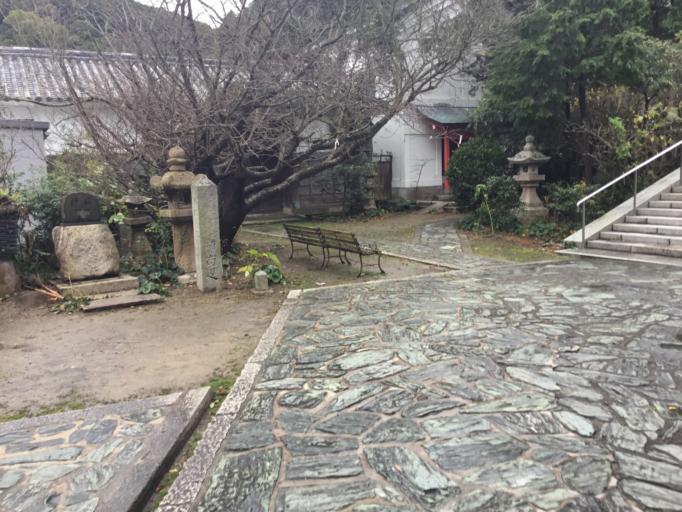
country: JP
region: Wakayama
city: Minato
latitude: 34.2738
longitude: 135.0668
